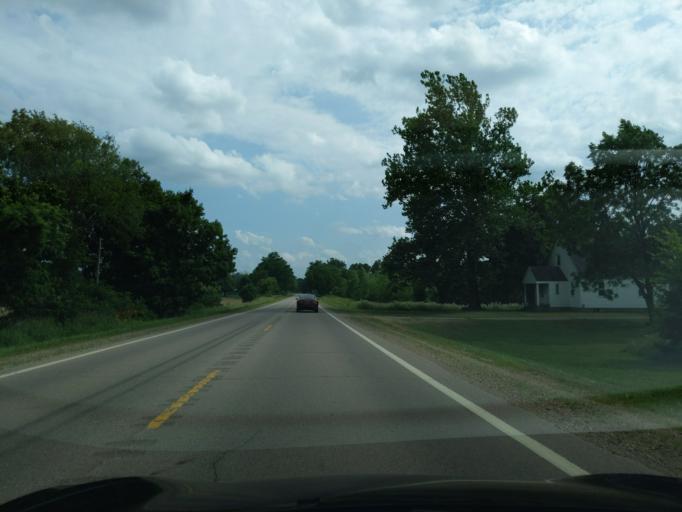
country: US
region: Michigan
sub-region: Eaton County
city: Eaton Rapids
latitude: 42.4688
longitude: -84.6596
